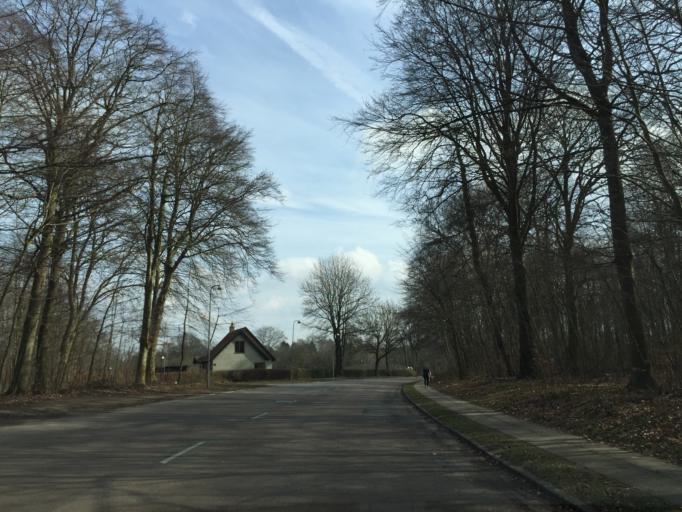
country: DK
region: South Denmark
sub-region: Odense Kommune
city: Stige
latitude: 55.4163
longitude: 10.4130
